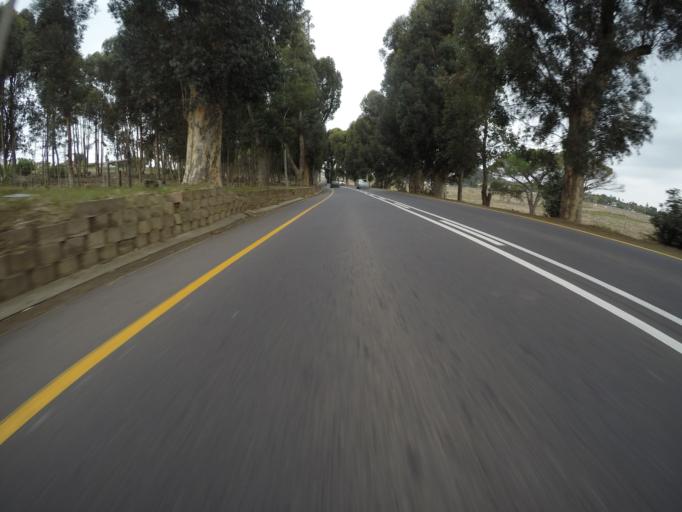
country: ZA
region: Western Cape
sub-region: City of Cape Town
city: Kraaifontein
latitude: -33.8436
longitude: 18.6303
